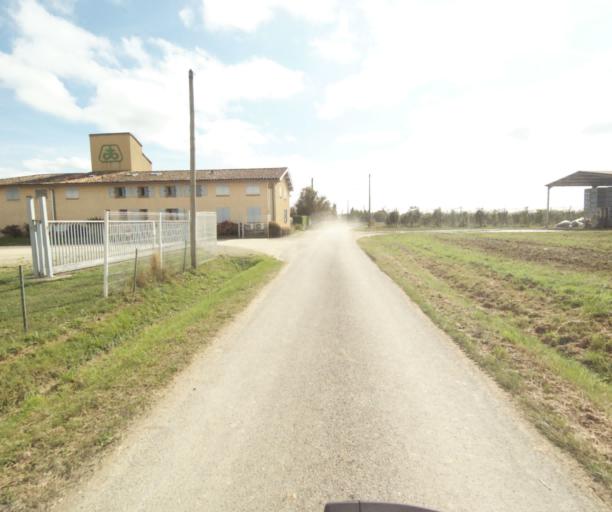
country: FR
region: Midi-Pyrenees
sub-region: Departement du Tarn-et-Garonne
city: Montech
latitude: 43.9426
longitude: 1.2062
